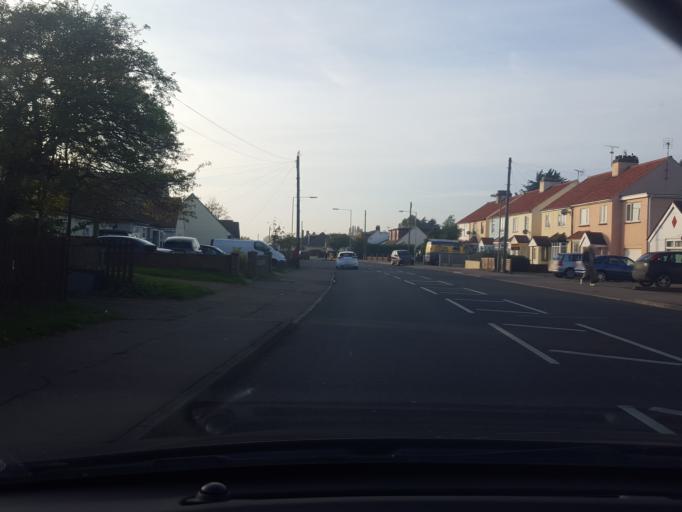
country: GB
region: England
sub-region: Essex
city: Frinton-on-Sea
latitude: 51.8418
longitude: 1.2263
